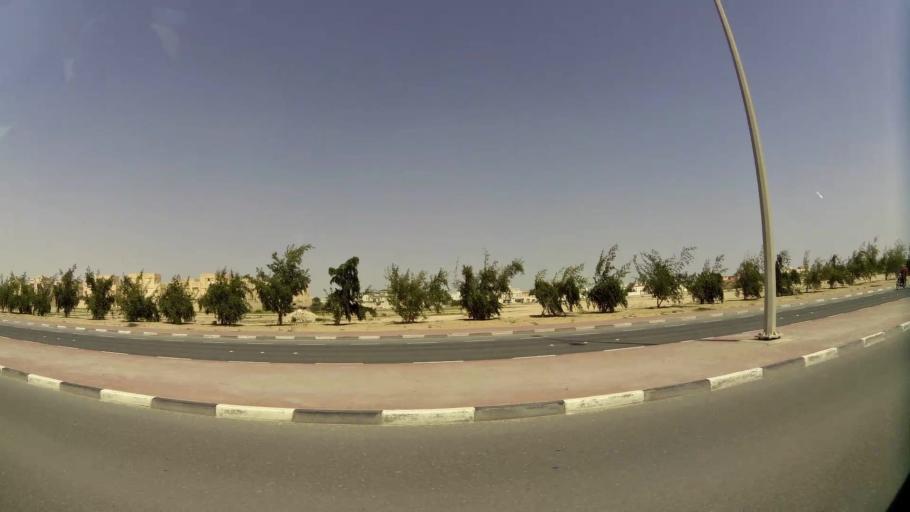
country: QA
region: Baladiyat Umm Salal
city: Umm Salal Muhammad
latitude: 25.3890
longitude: 51.4223
